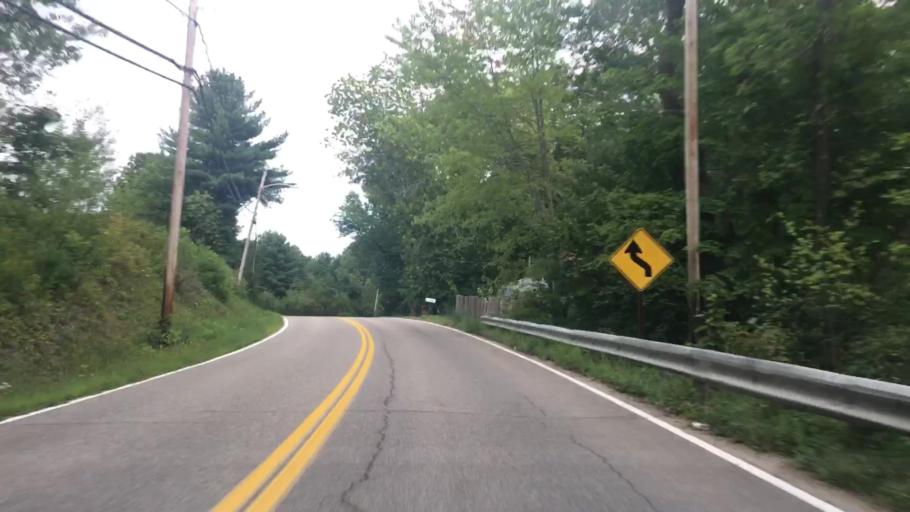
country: US
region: Maine
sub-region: York County
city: Biddeford
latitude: 43.5033
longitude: -70.4741
